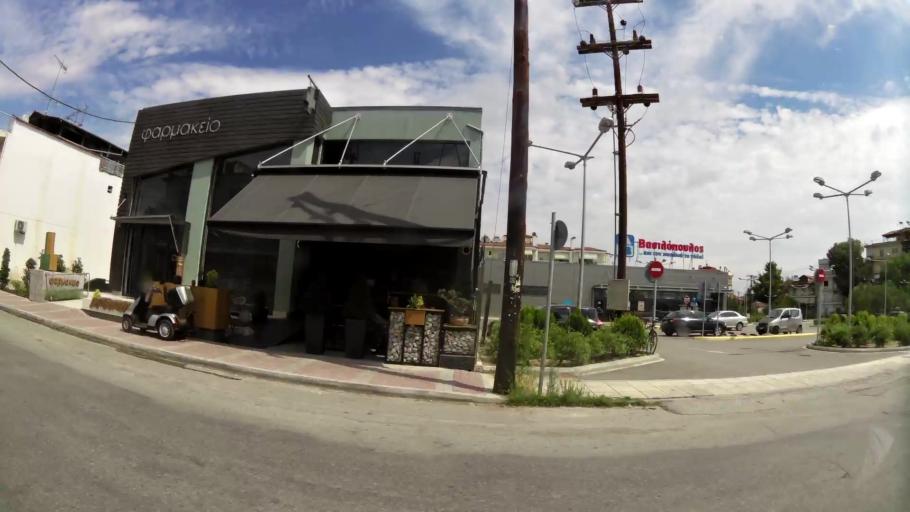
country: GR
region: Central Macedonia
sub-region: Nomos Pierias
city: Katerini
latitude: 40.2720
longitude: 22.4948
